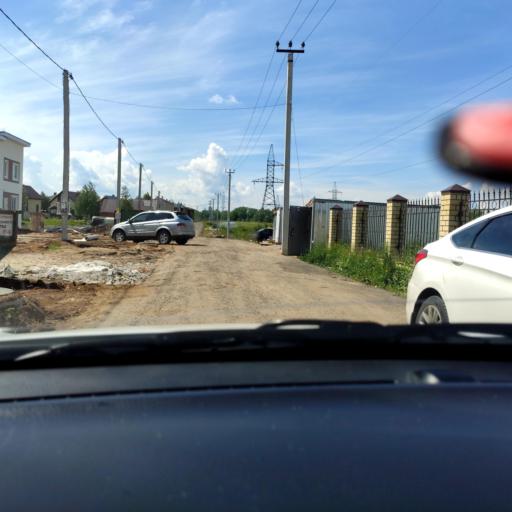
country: RU
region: Tatarstan
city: Stolbishchi
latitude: 55.7253
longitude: 49.3128
